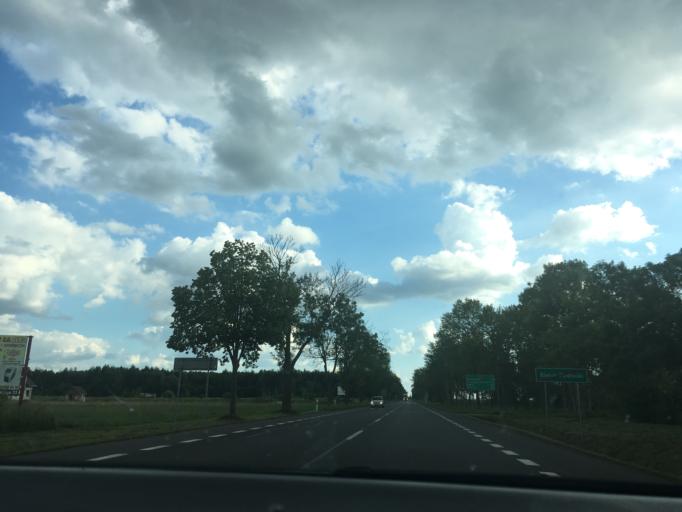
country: PL
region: Podlasie
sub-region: Powiat bielski
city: Bielsk Podlaski
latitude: 52.7511
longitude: 23.1722
